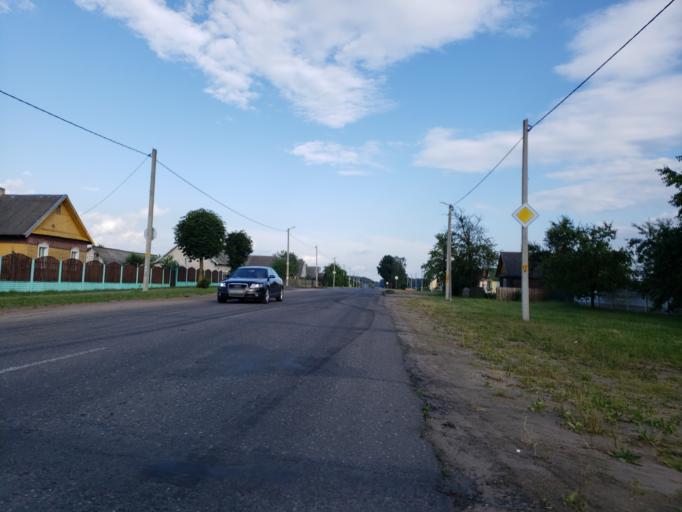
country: BY
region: Minsk
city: Chervyen'
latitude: 53.7019
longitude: 28.4427
